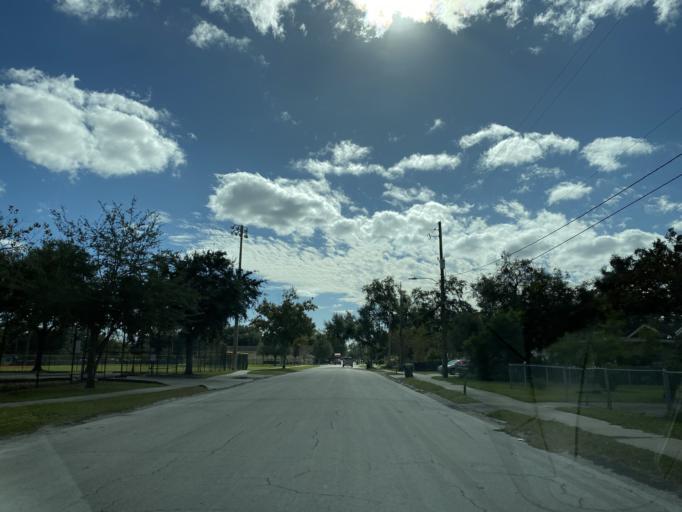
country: US
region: Florida
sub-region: Orange County
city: Orlando
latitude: 28.5251
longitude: -81.3909
